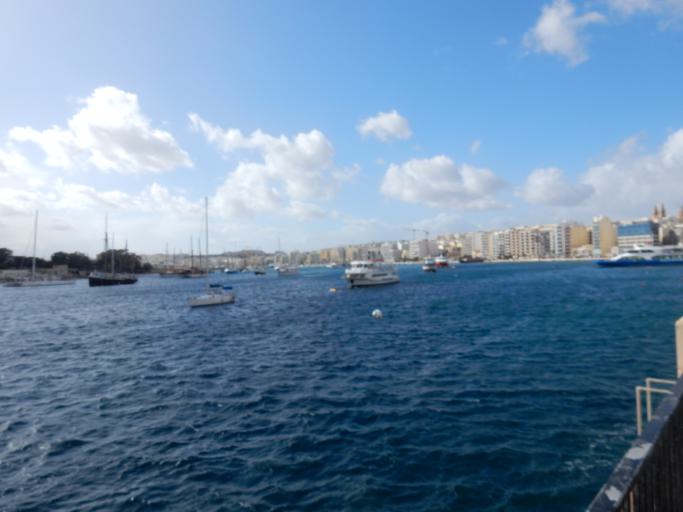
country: MT
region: Tas-Sliema
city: Sliema
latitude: 35.9070
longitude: 14.5079
